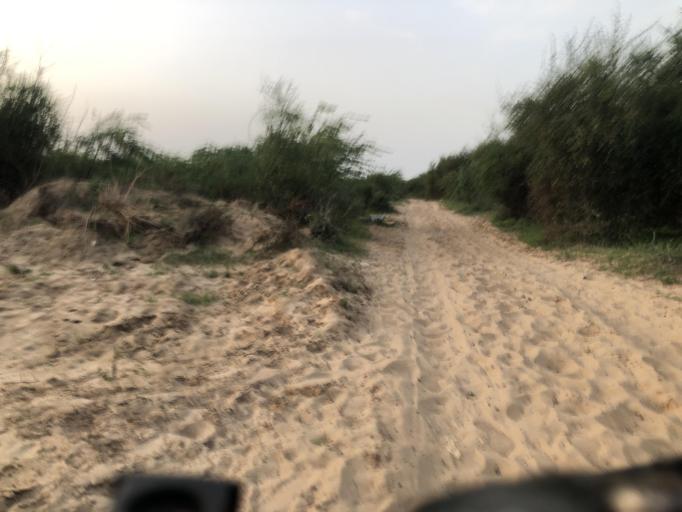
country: SN
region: Saint-Louis
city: Saint-Louis
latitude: 16.0570
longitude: -16.4318
